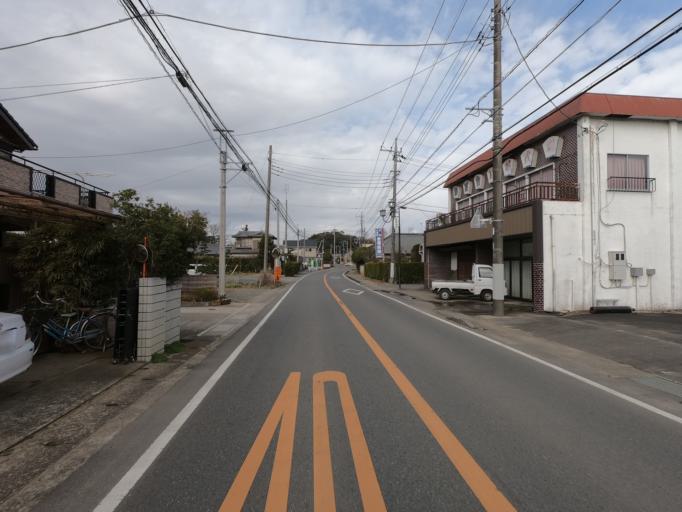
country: JP
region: Ibaraki
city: Inashiki
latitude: 36.0895
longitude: 140.4248
